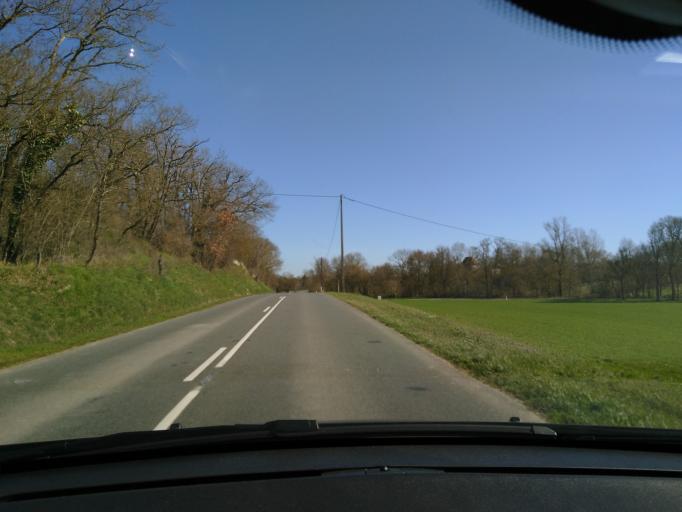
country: FR
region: Aquitaine
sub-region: Departement du Lot-et-Garonne
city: Cancon
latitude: 44.5353
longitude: 0.6628
